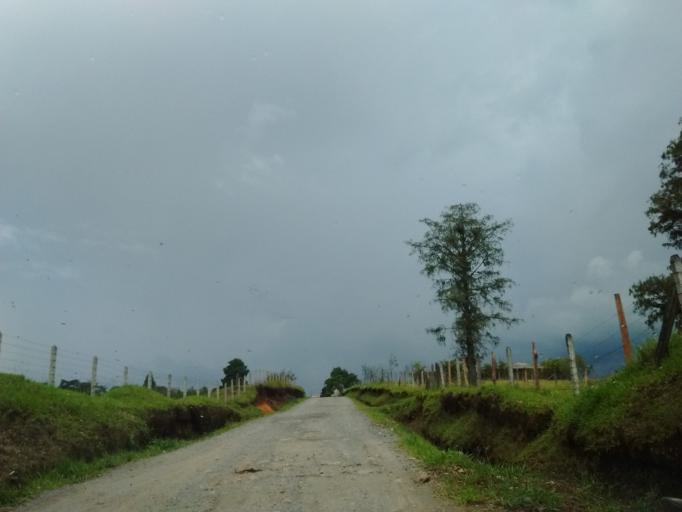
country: CO
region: Cauca
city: Cajibio
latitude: 2.5494
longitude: -76.6256
